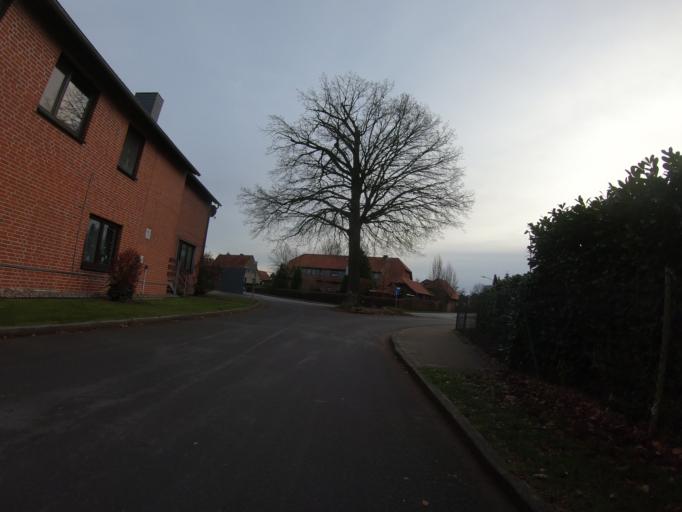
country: DE
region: Lower Saxony
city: Isenbuttel
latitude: 52.4335
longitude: 10.5838
